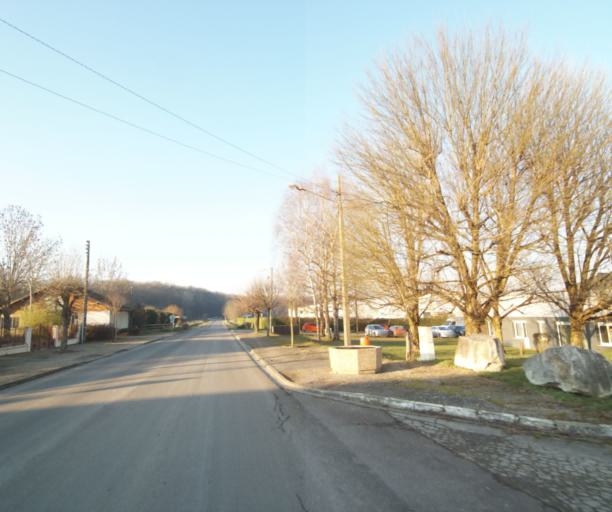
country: FR
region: Champagne-Ardenne
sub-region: Departement de la Haute-Marne
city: Bienville
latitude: 48.5889
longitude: 5.0345
